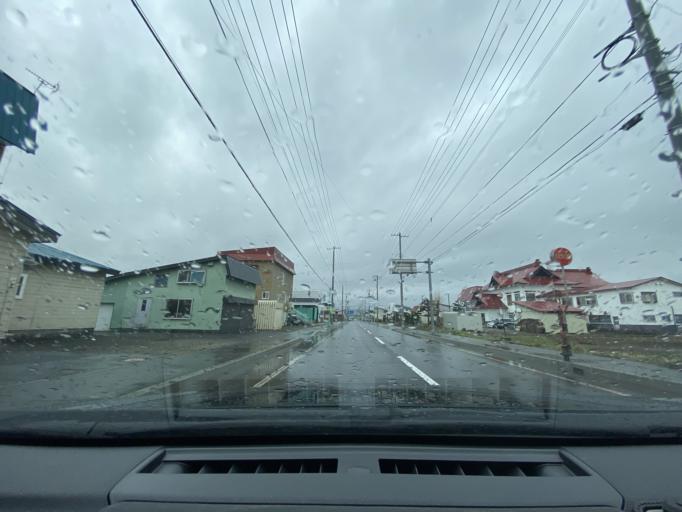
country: JP
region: Hokkaido
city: Fukagawa
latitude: 43.8086
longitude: 141.9447
